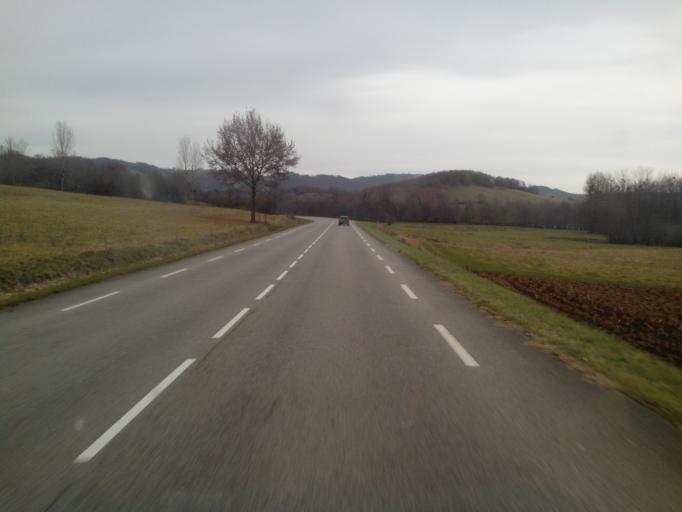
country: FR
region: Midi-Pyrenees
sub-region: Departement de l'Ariege
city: Montjoie-en-Couserans
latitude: 43.0075
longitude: 1.3637
